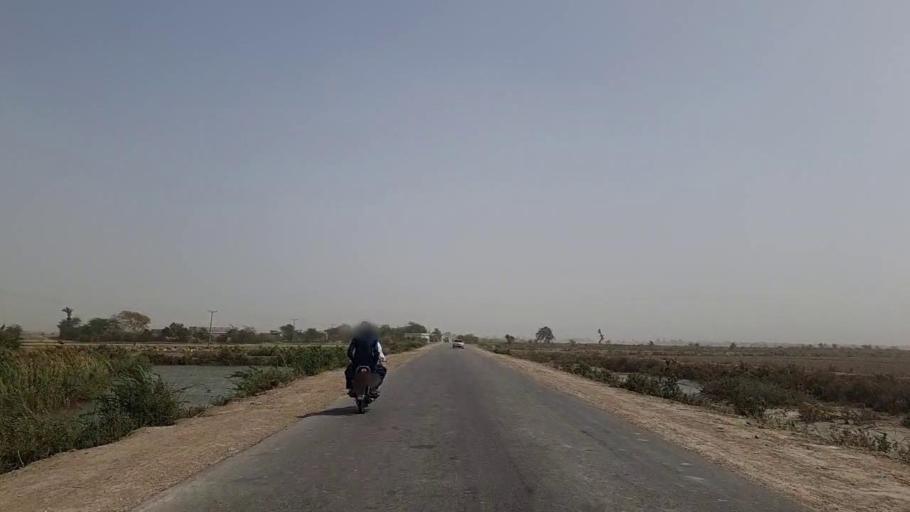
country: PK
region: Sindh
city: Talhar
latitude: 24.8778
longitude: 68.8340
